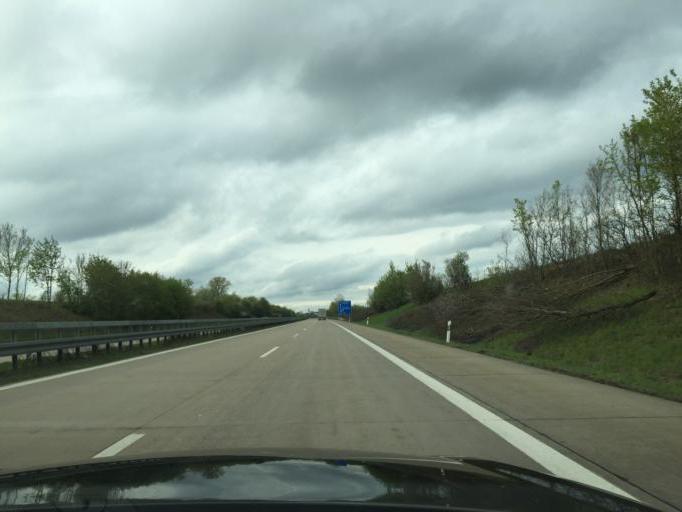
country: DE
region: Baden-Wuerttemberg
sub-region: Regierungsbezirk Stuttgart
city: Ellwangen
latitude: 48.9469
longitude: 10.1904
